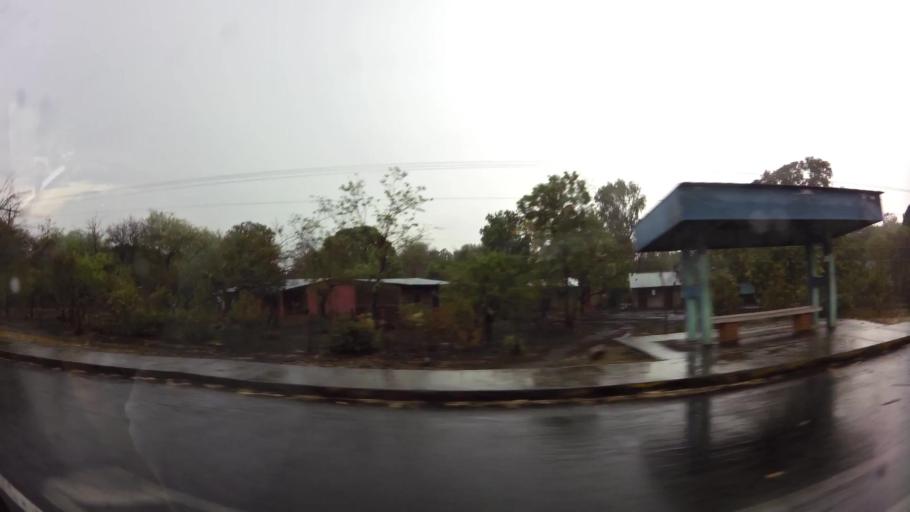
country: NI
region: Leon
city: Telica
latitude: 12.5362
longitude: -86.8441
